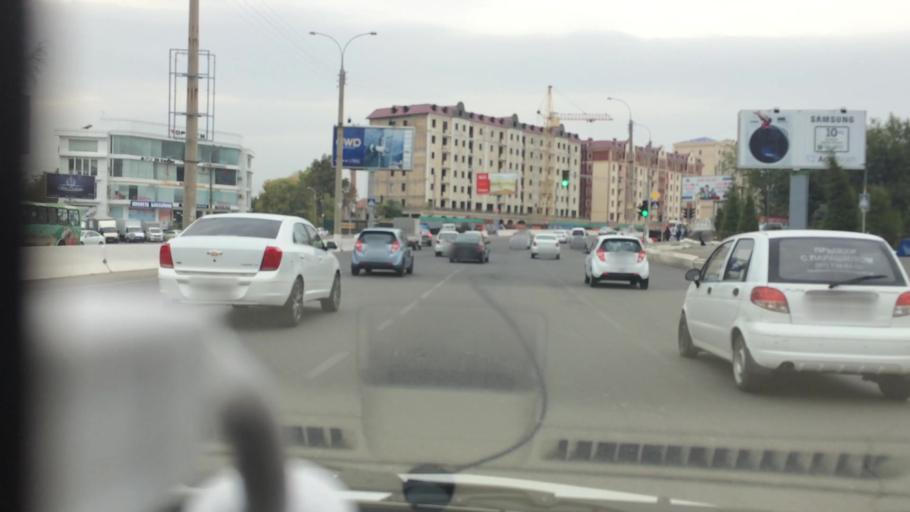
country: UZ
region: Toshkent
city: Salor
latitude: 41.3147
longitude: 69.3275
